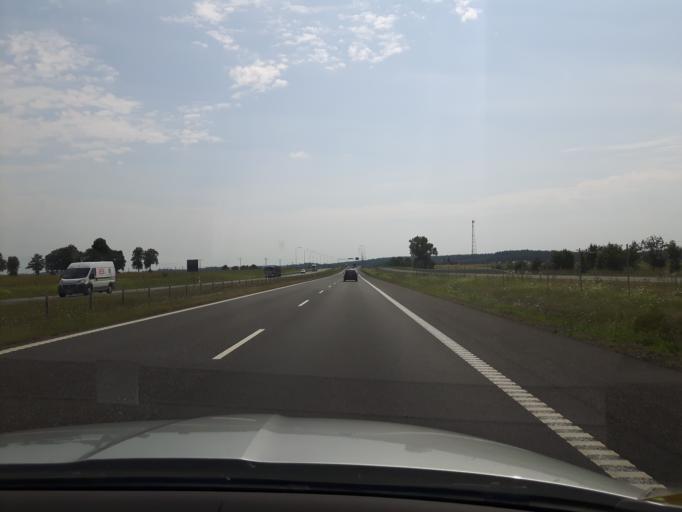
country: PL
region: Warmian-Masurian Voivodeship
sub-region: Powiat nidzicki
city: Nidzica
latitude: 53.4196
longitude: 20.3366
